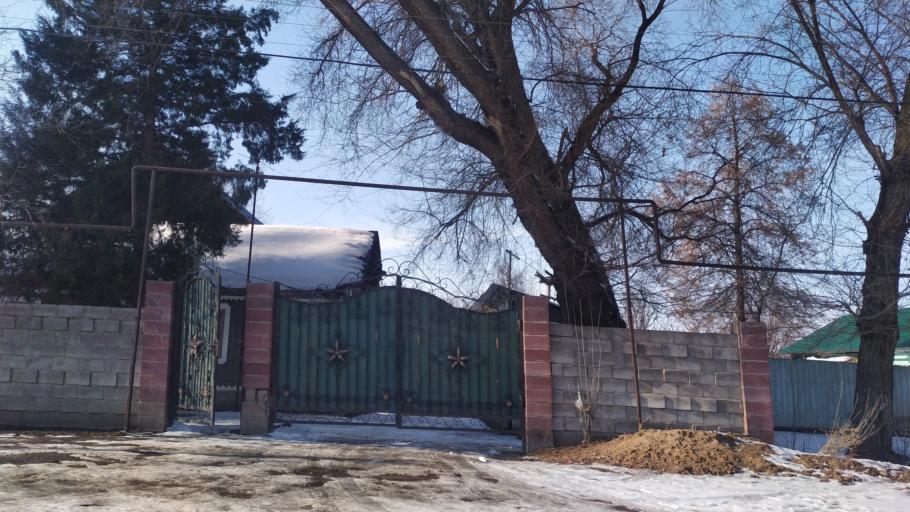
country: KZ
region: Almaty Oblysy
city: Burunday
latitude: 43.2479
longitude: 76.4342
